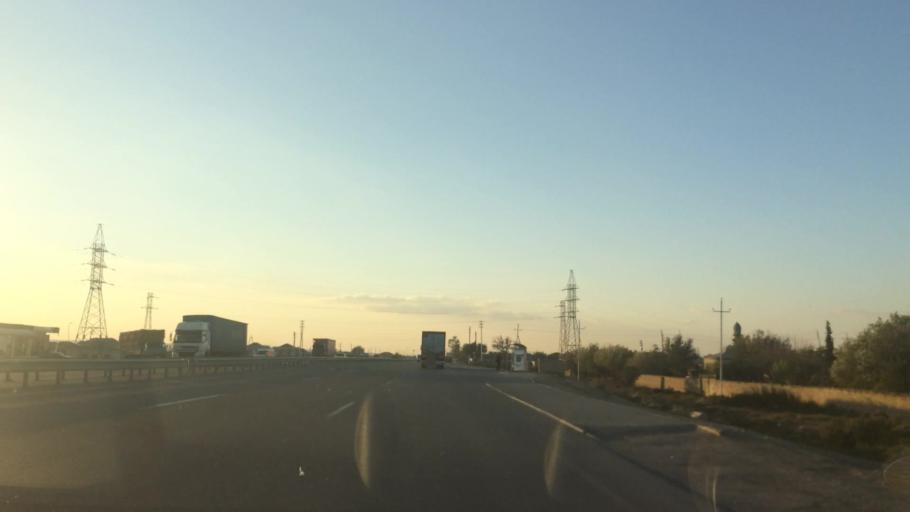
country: AZ
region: Baki
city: Qobustan
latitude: 39.9692
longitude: 49.2682
